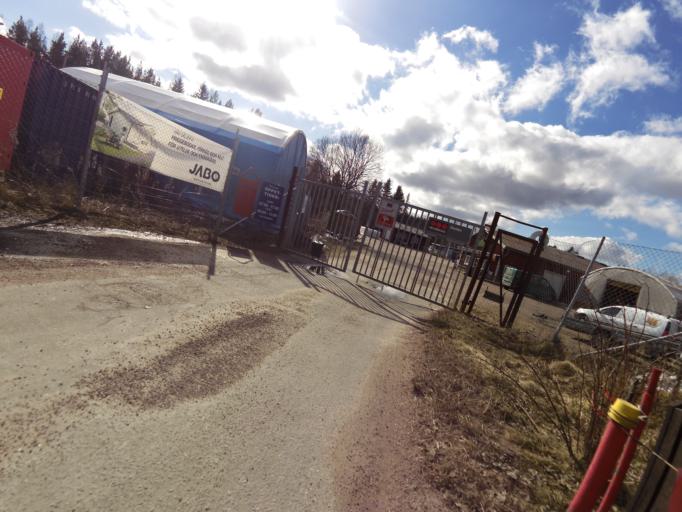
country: SE
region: Gaevleborg
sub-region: Hofors Kommun
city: Hofors
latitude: 60.5398
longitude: 16.2870
